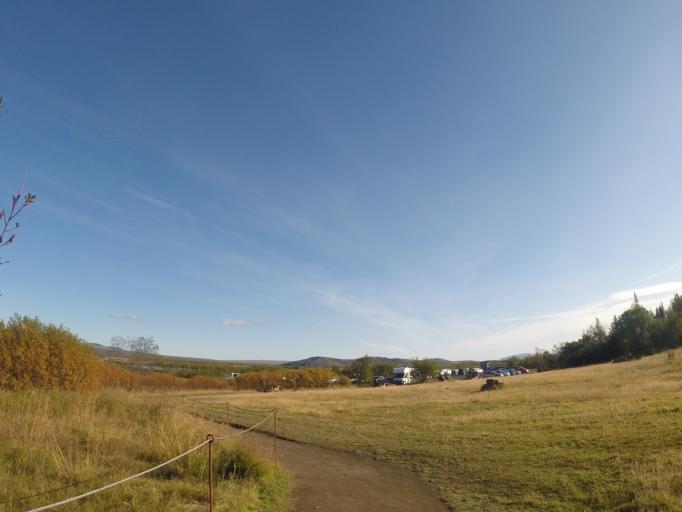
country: IS
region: South
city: Hveragerdi
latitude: 64.2564
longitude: -21.1253
